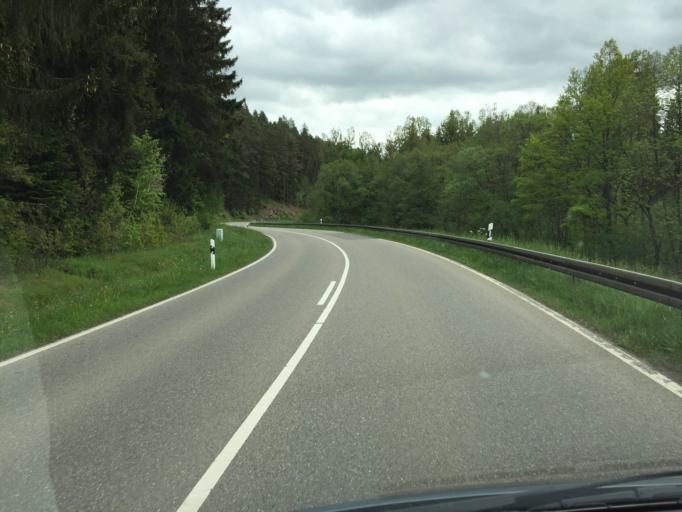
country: DE
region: Baden-Wuerttemberg
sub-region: Freiburg Region
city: Unterkirnach
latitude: 48.0718
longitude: 8.4022
